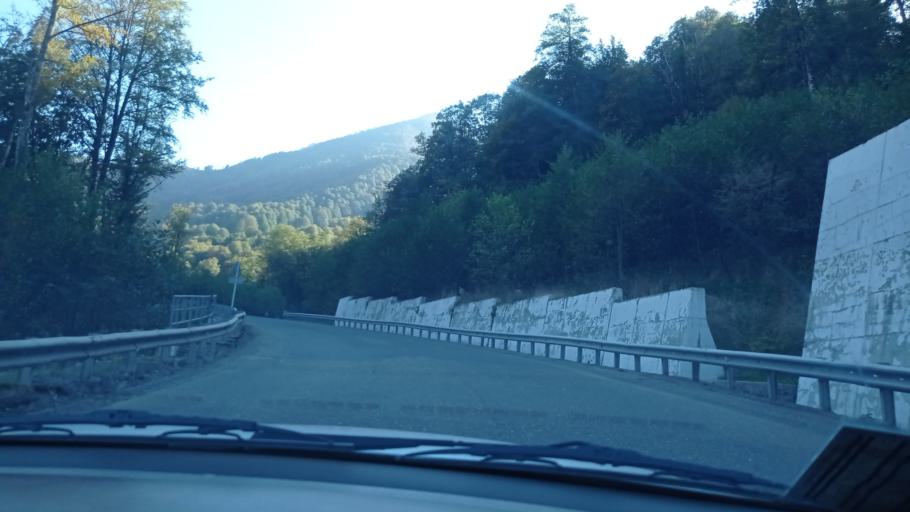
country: RU
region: Krasnodarskiy
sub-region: Sochi City
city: Krasnaya Polyana
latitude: 43.6614
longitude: 40.2997
